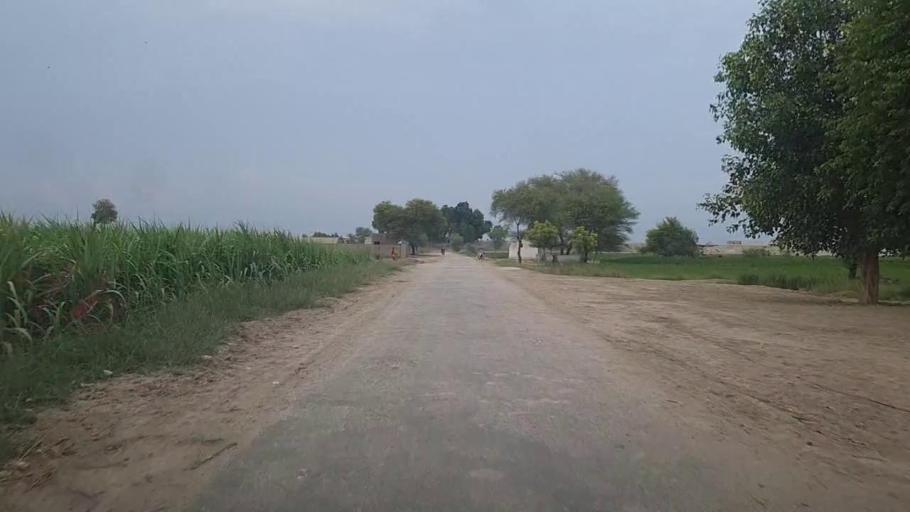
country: PK
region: Sindh
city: Kashmor
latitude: 28.3761
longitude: 69.7836
